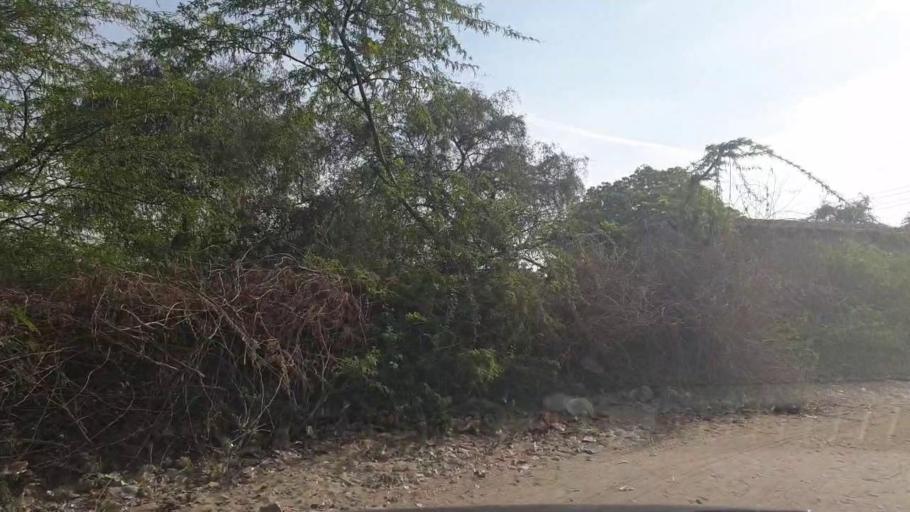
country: PK
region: Sindh
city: Umarkot
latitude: 25.3108
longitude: 69.7049
